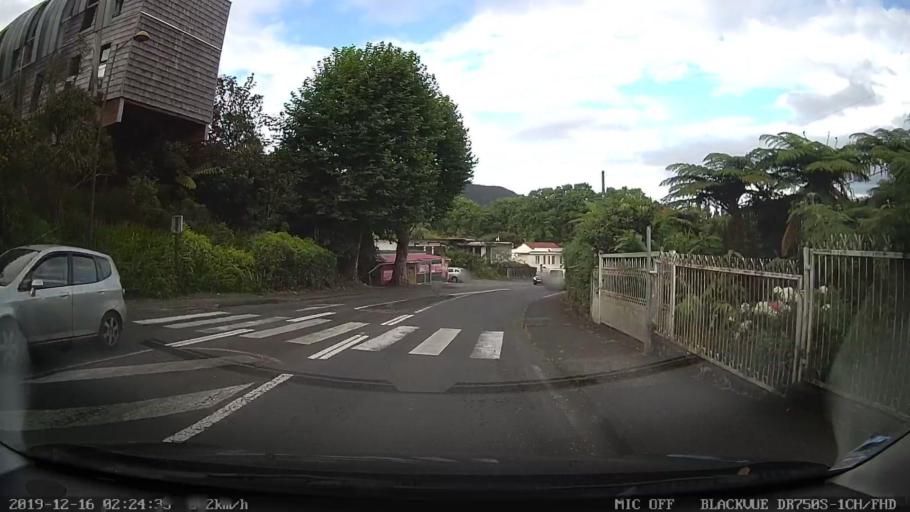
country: RE
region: Reunion
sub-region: Reunion
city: Saint-Benoit
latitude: -21.1367
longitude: 55.6245
